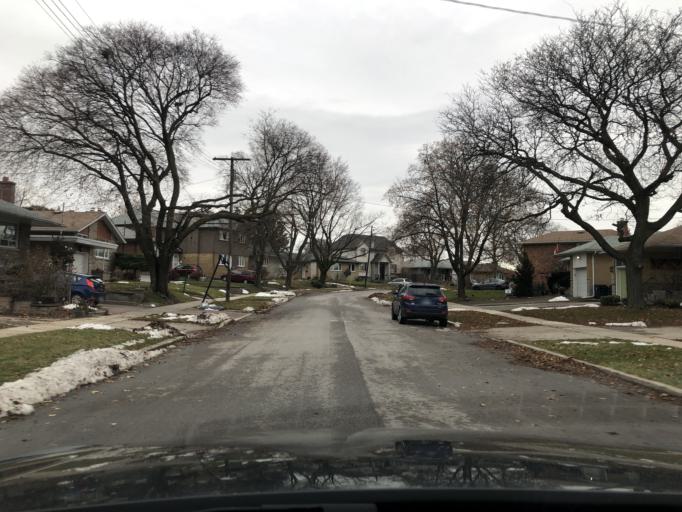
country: CA
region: Ontario
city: Etobicoke
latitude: 43.6912
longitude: -79.5327
